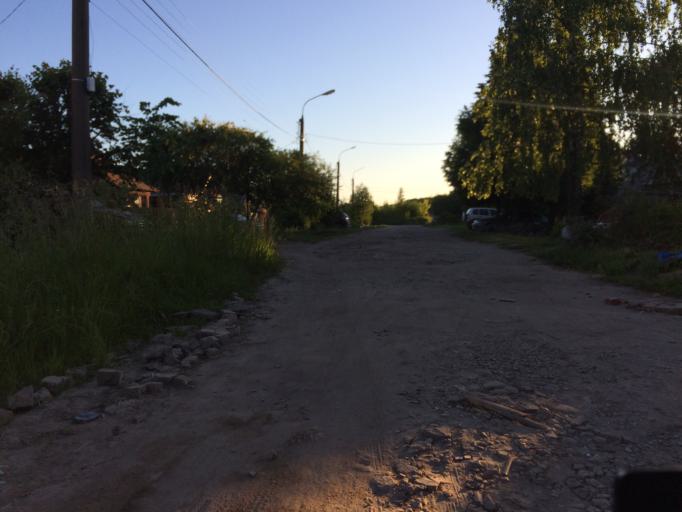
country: RU
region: Mariy-El
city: Yoshkar-Ola
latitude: 56.6541
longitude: 47.8974
